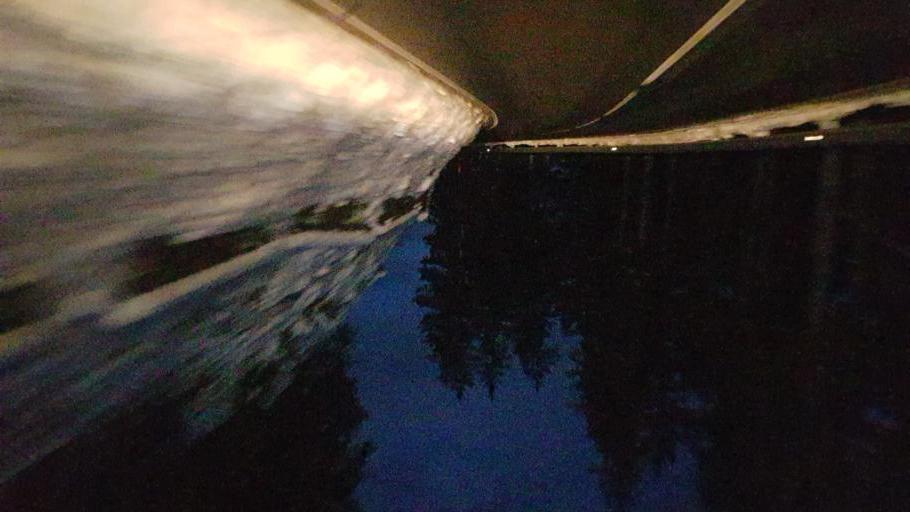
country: AT
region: Salzburg
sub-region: Politischer Bezirk Sankt Johann im Pongau
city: Forstau
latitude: 47.3819
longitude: 13.4958
